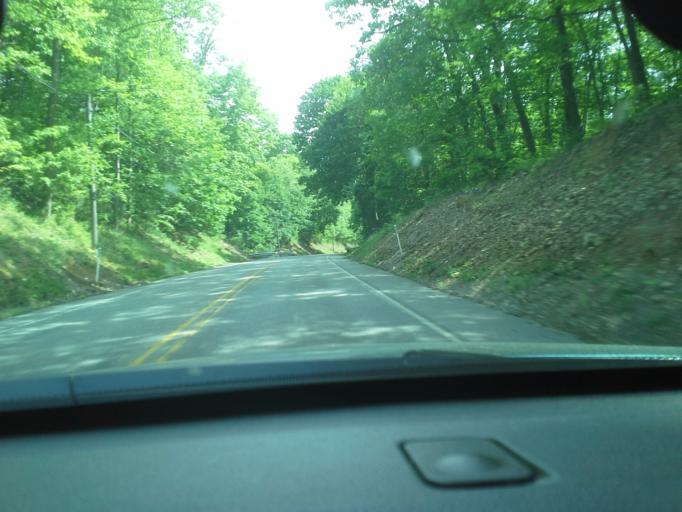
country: US
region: Pennsylvania
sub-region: Fulton County
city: McConnellsburg
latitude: 39.9119
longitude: -77.9664
